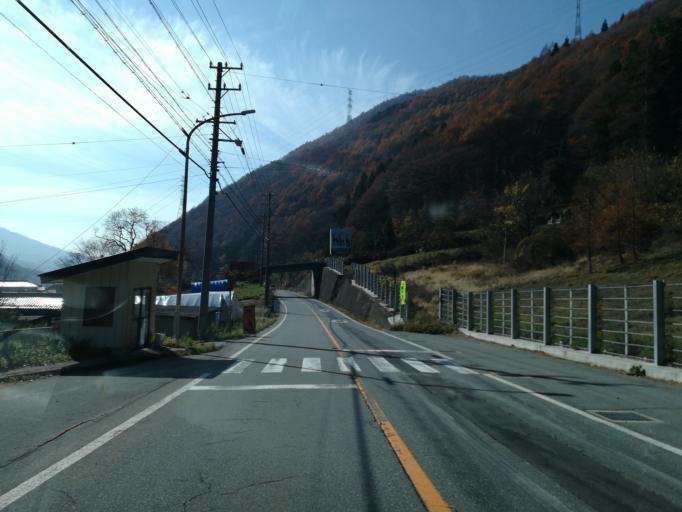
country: JP
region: Nagano
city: Ueda
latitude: 36.4788
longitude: 138.3473
